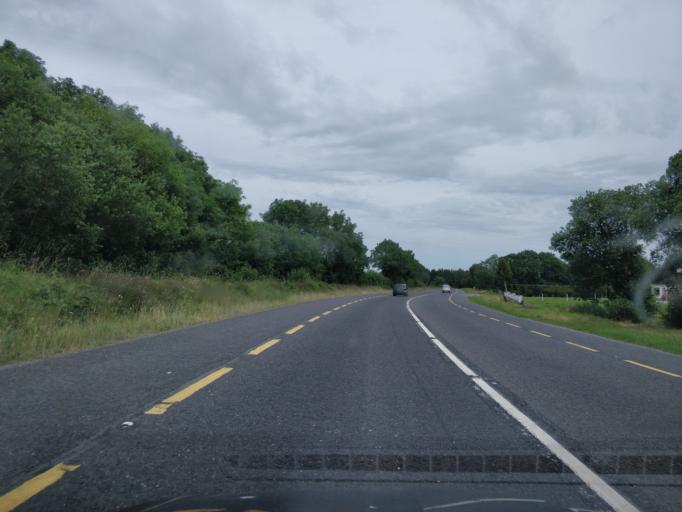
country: IE
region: Leinster
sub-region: Uibh Fhaili
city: Birr
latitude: 53.1231
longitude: -7.8823
